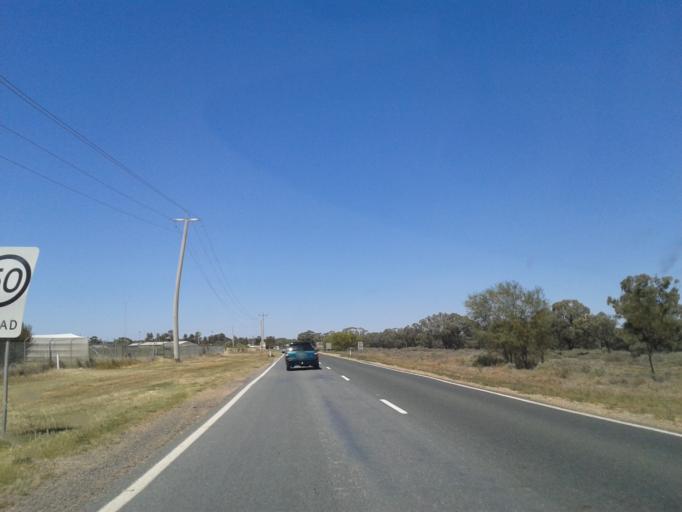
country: AU
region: New South Wales
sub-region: Wentworth
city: Gol Gol
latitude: -34.5708
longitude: 142.7319
